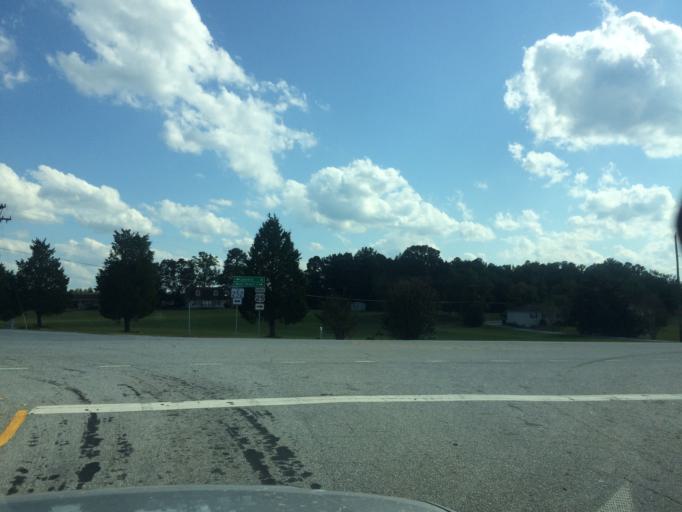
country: US
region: South Carolina
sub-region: Greenwood County
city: Ware Shoals
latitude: 34.4258
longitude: -82.2382
